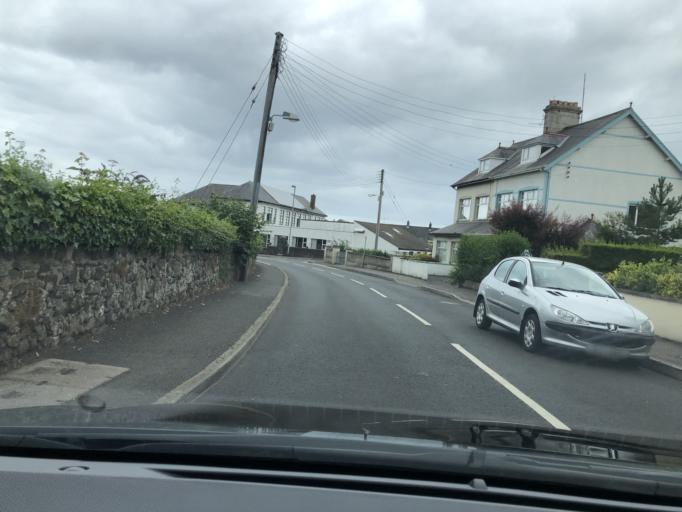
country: GB
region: Northern Ireland
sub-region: Larne District
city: Larne
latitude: 54.8491
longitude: -5.8249
